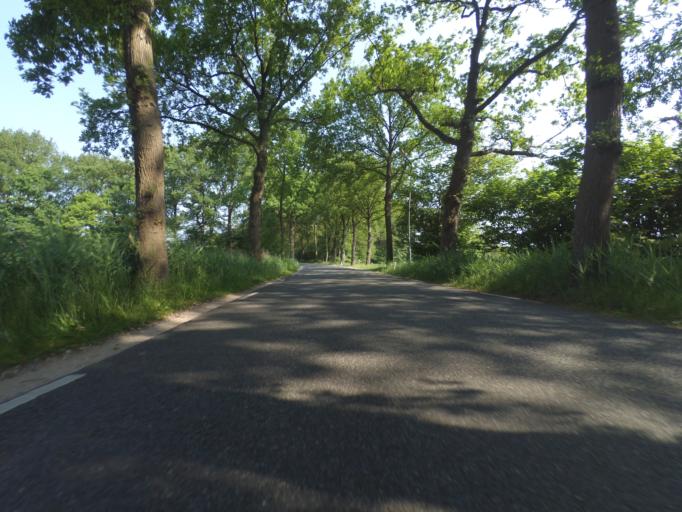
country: NL
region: Utrecht
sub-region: Gemeente Leusden
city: Leusden
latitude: 52.1090
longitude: 5.4759
